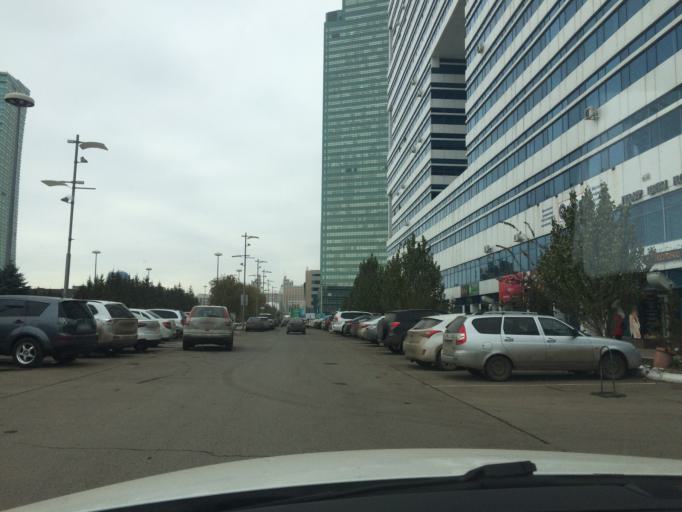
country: KZ
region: Astana Qalasy
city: Astana
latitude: 51.1294
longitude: 71.4269
